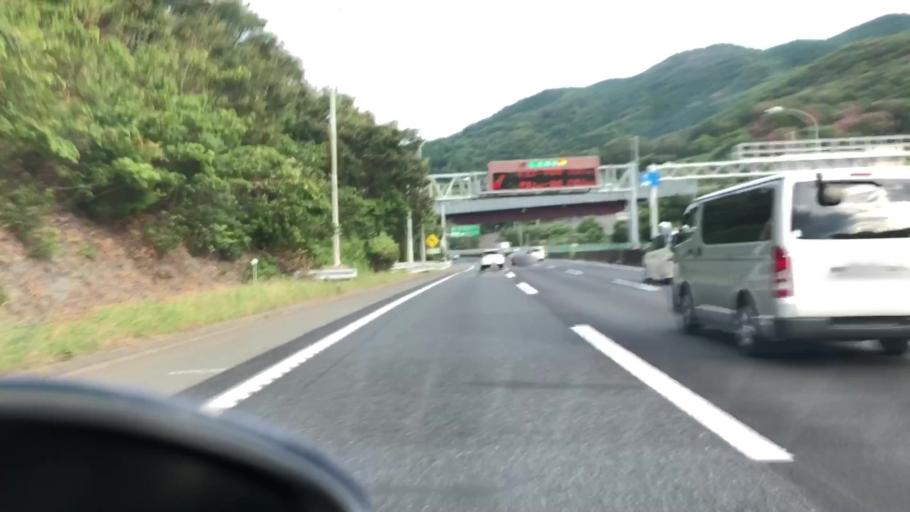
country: JP
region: Hyogo
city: Sandacho
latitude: 34.8361
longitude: 135.2597
